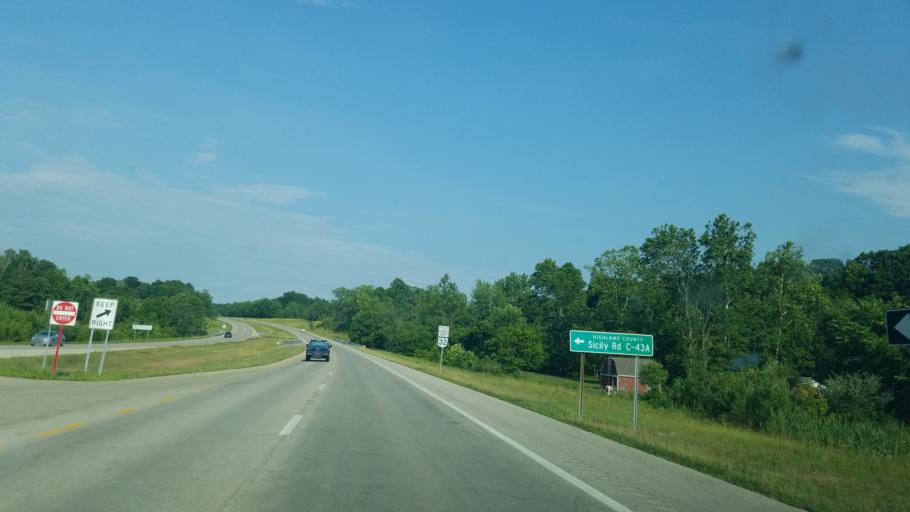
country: US
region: Ohio
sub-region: Brown County
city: Mount Orab
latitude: 39.0201
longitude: -83.8631
